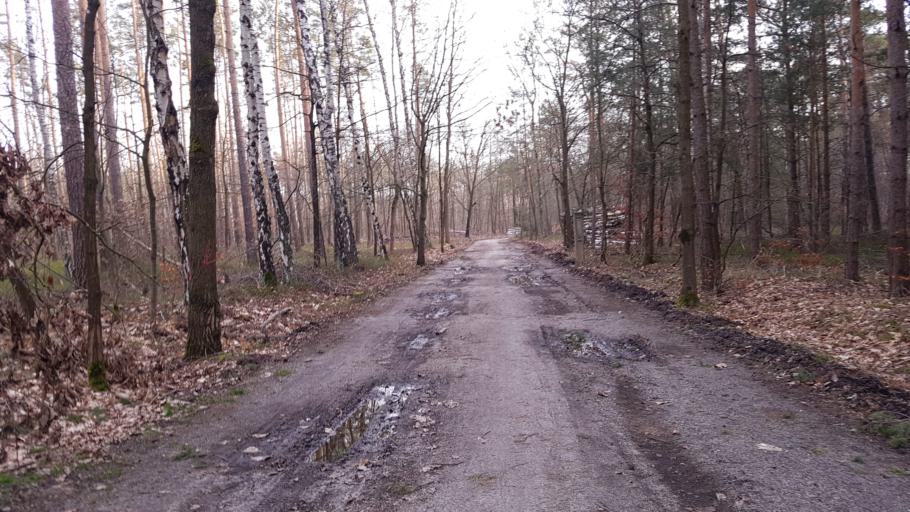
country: DE
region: Brandenburg
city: Finsterwalde
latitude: 51.6285
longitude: 13.6817
